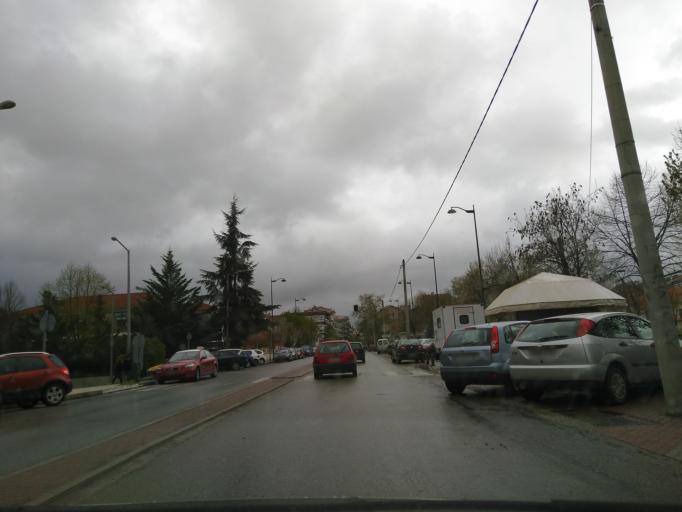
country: GR
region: West Macedonia
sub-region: Nomos Grevenon
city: Grevena
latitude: 40.0856
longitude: 21.4378
